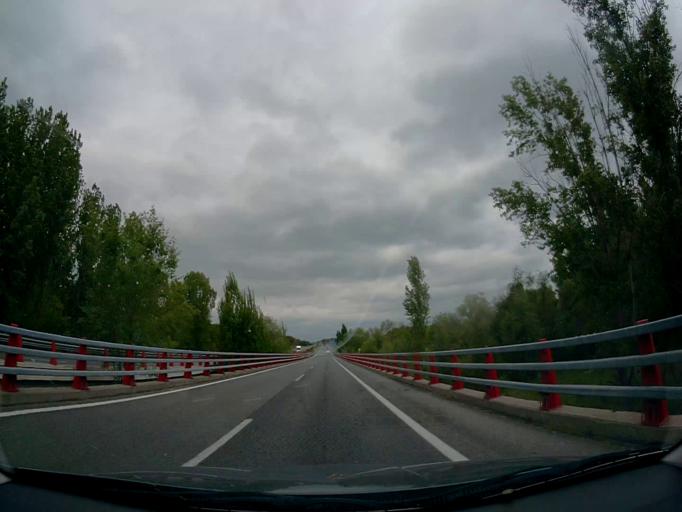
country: ES
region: Madrid
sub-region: Provincia de Madrid
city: Villaviciosa de Odon
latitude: 40.3688
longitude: -3.9482
